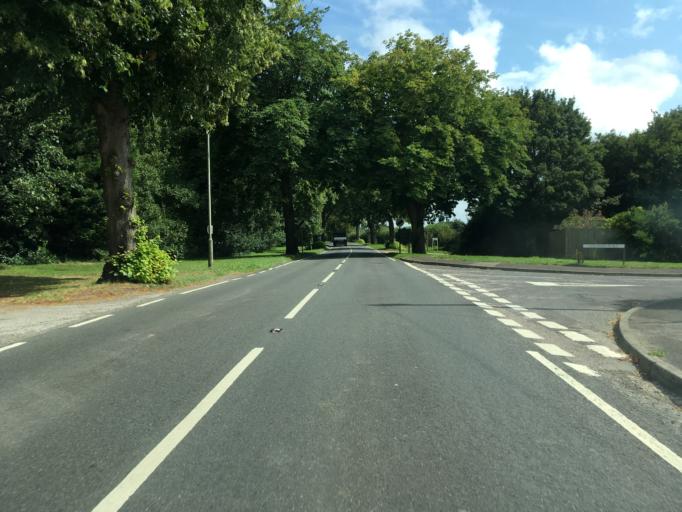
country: GB
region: England
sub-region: Kent
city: Tenterden
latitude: 51.0675
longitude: 0.7072
